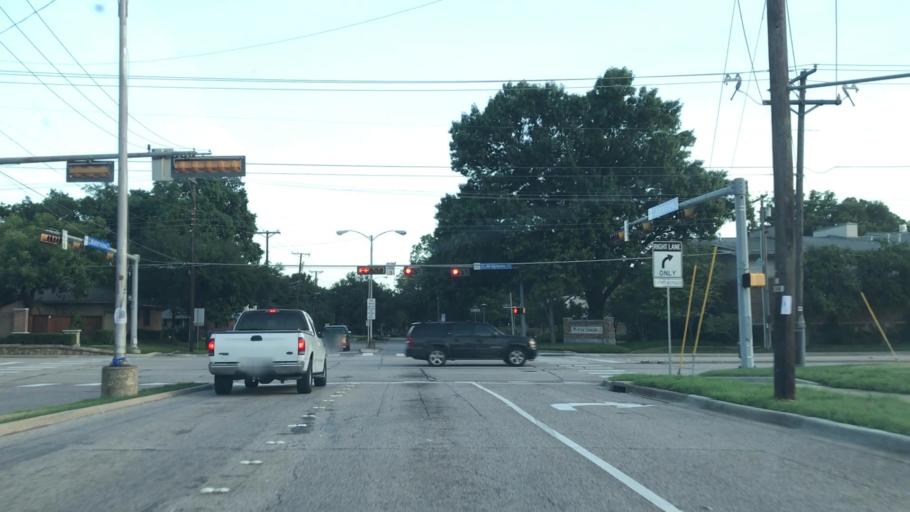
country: US
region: Texas
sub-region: Dallas County
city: Richardson
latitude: 32.9627
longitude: -96.7559
